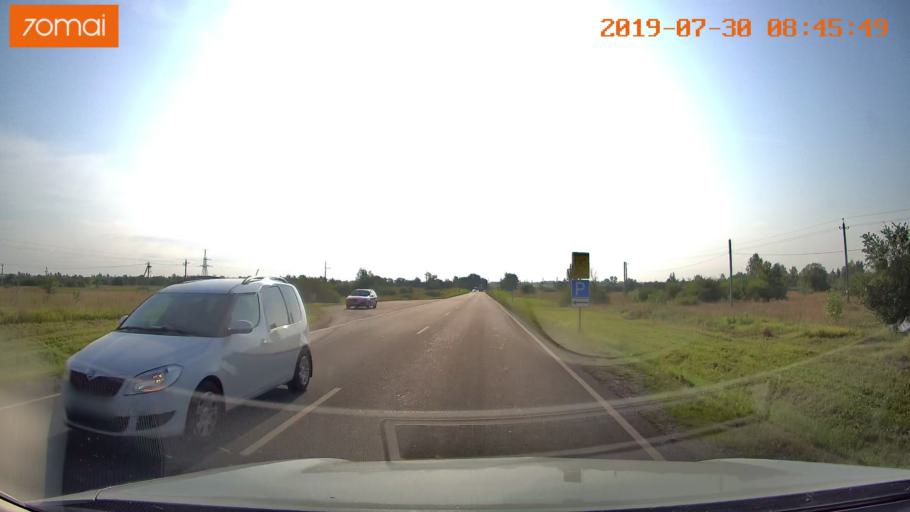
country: RU
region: Kaliningrad
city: Chernyakhovsk
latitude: 54.6253
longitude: 21.8713
